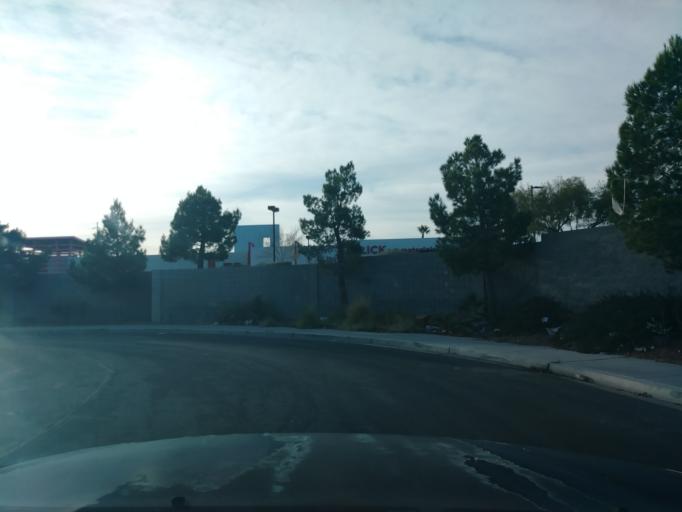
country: US
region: Nevada
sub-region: Clark County
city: Spring Valley
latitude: 36.1603
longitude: -115.2311
